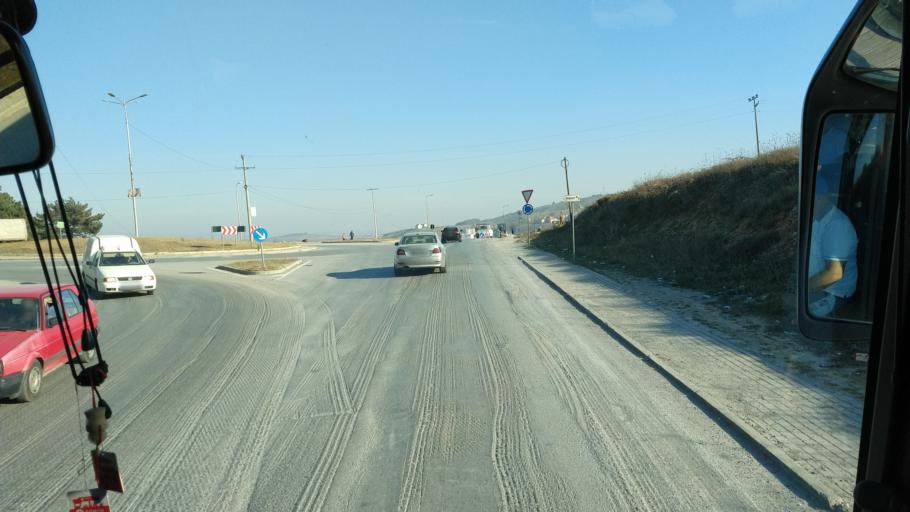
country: XK
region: Ferizaj
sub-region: Komuna e Shtimes
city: Shtime
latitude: 42.4376
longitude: 21.0221
